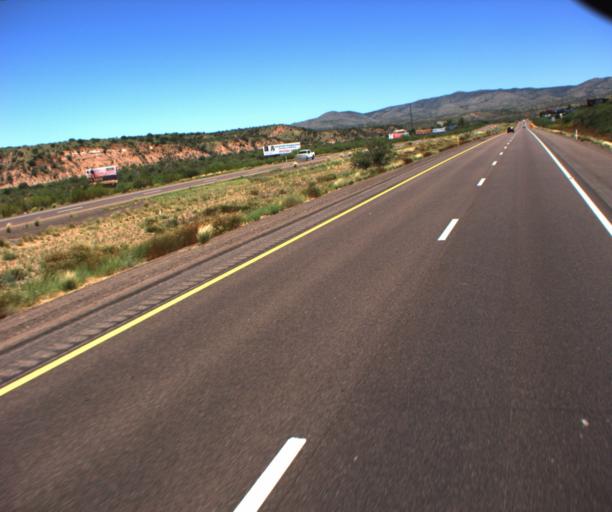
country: US
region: Arizona
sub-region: Gila County
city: Payson
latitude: 34.0956
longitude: -111.3534
